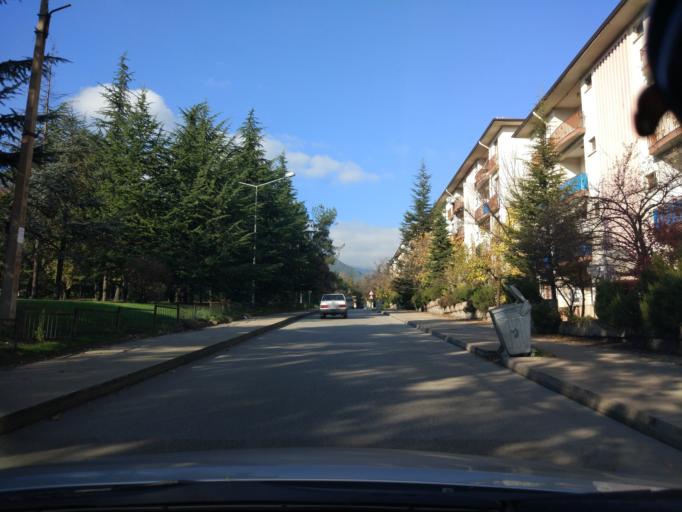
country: TR
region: Karabuk
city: Karabuk
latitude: 41.1983
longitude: 32.6228
